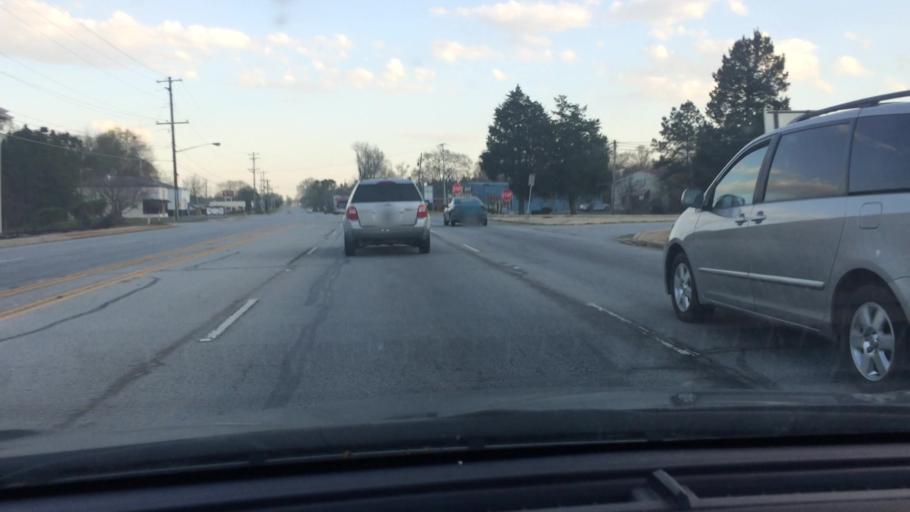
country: US
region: South Carolina
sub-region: Newberry County
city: Newberry
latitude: 34.2691
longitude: -81.5886
